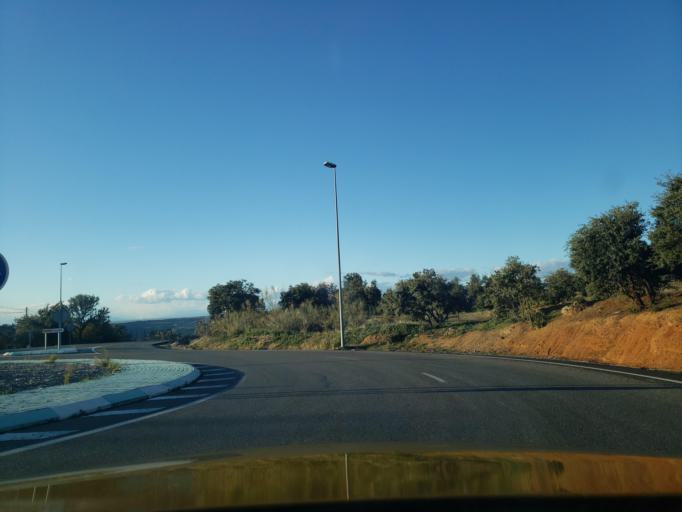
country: ES
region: Castille-La Mancha
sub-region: Province of Toledo
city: Toledo
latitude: 39.8457
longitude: -4.0230
